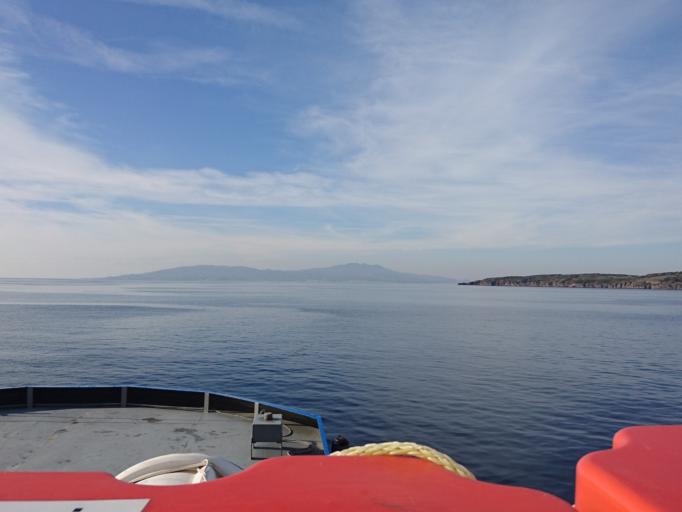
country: TR
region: Mugla
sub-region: Bodrum
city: Bodrum
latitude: 37.0032
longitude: 27.4050
